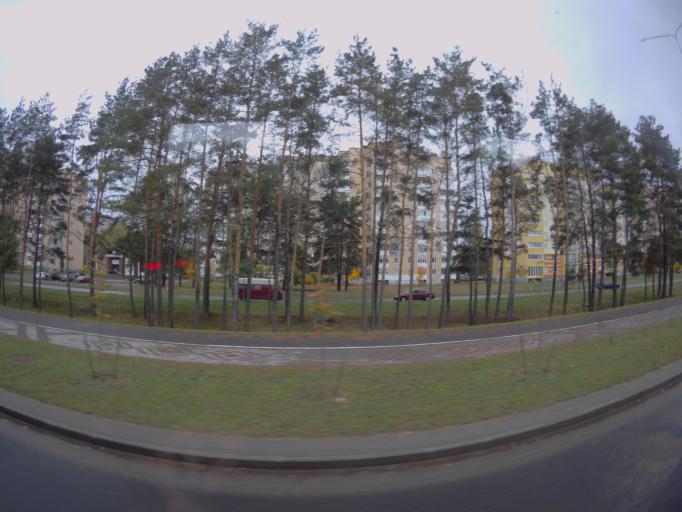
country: BY
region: Minsk
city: Horad Barysaw
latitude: 54.2065
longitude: 28.4842
